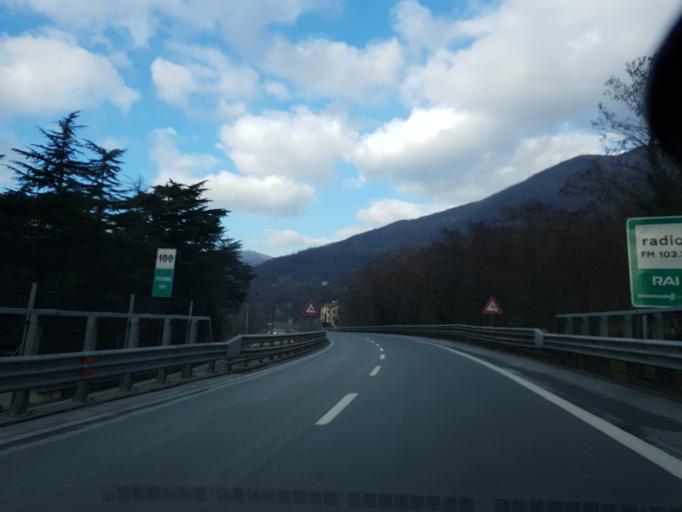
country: IT
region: Liguria
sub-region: Provincia di Genova
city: Isola del Cantone
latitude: 44.6456
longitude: 8.9595
